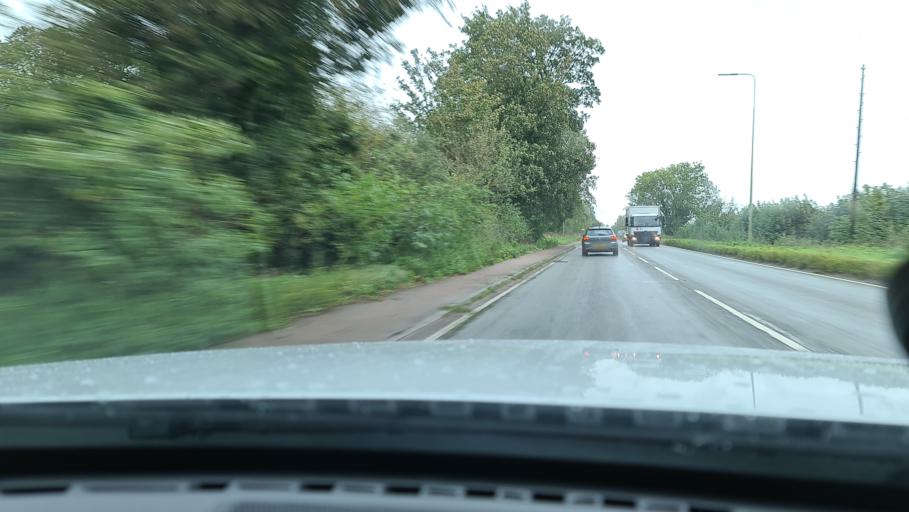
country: GB
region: England
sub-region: Oxfordshire
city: Adderbury
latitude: 52.0277
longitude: -1.3131
